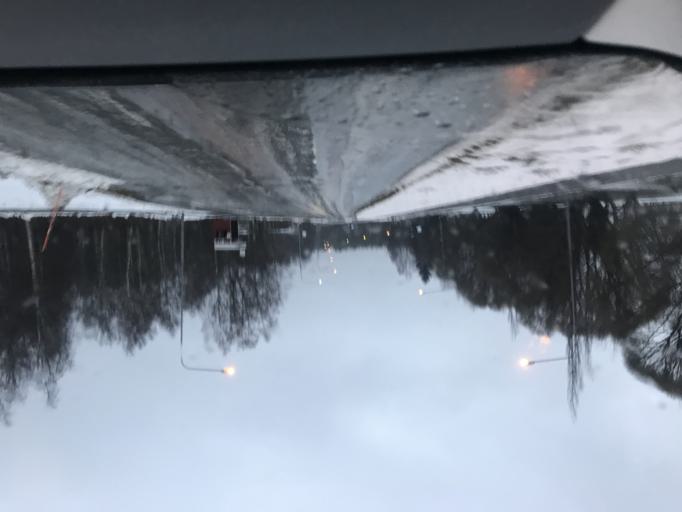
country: SE
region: Norrbotten
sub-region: Lulea Kommun
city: Sodra Sunderbyn
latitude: 65.6533
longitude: 21.9655
